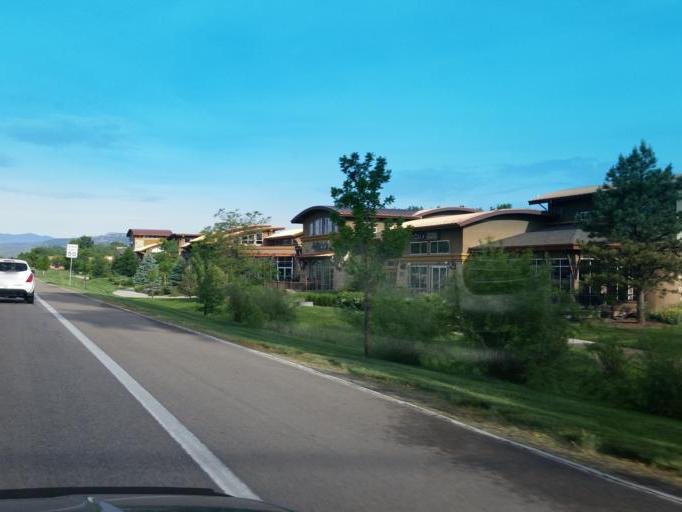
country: US
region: Colorado
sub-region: Larimer County
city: Fort Collins
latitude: 40.5234
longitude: -105.0324
